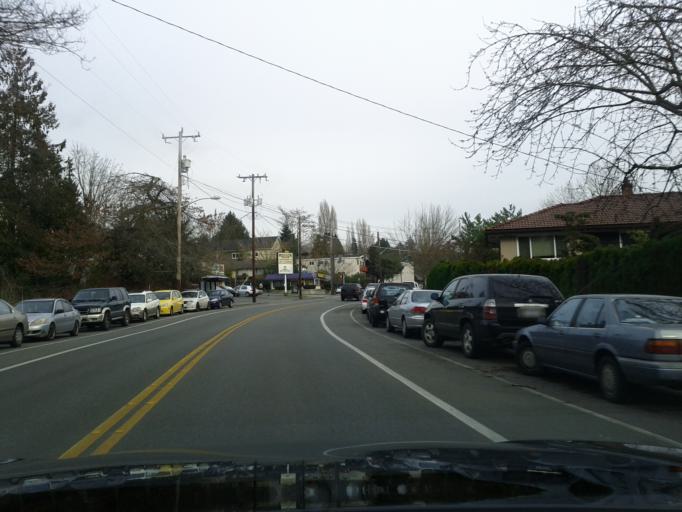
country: US
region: Washington
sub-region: King County
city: Seattle
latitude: 47.6684
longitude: -122.3019
